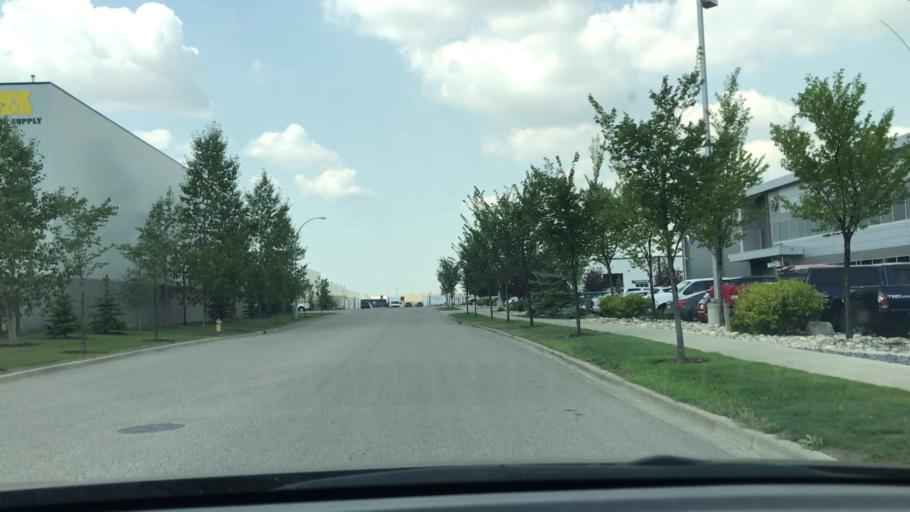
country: CA
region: Alberta
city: Edmonton
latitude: 53.4930
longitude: -113.4041
